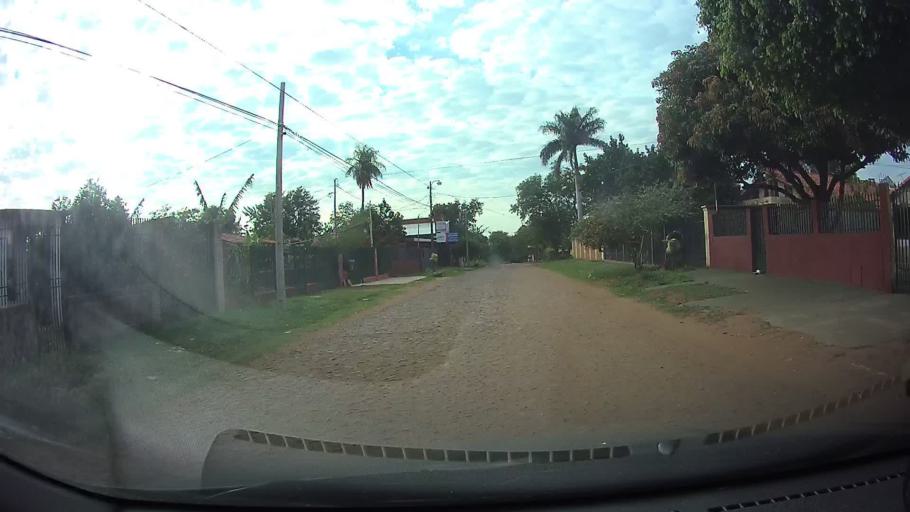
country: PY
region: Central
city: Limpio
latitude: -25.2509
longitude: -57.5049
